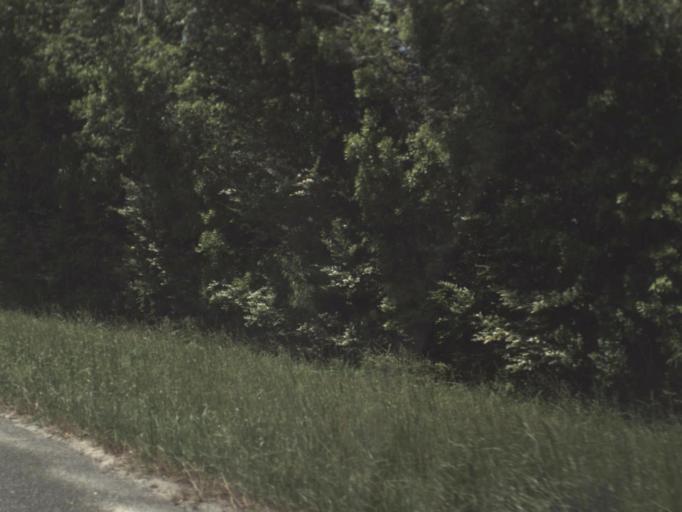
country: US
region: Florida
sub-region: Jefferson County
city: Monticello
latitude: 30.5791
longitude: -83.8702
